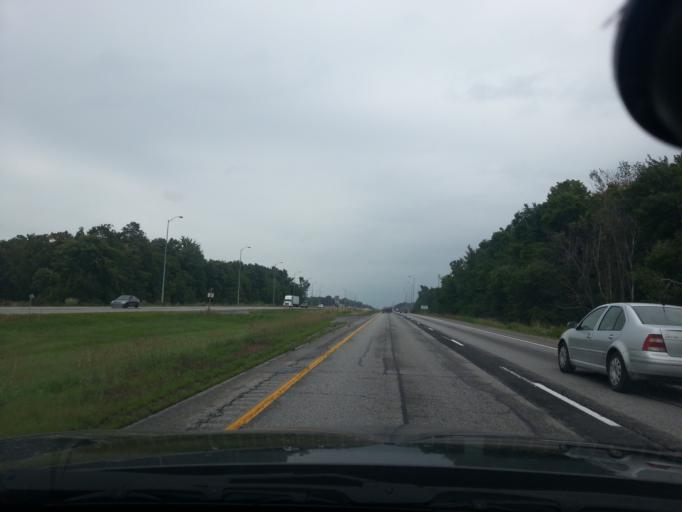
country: CA
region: Ontario
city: Gananoque
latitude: 44.3567
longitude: -76.0907
